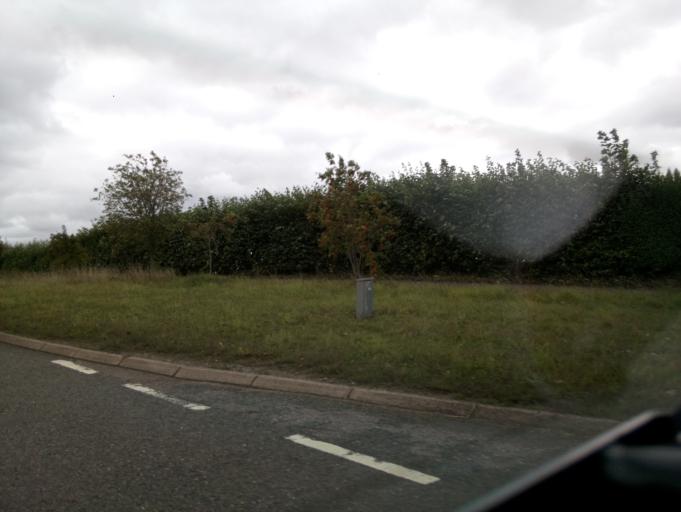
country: GB
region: England
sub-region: Devon
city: Heavitree
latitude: 50.7038
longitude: -3.4882
